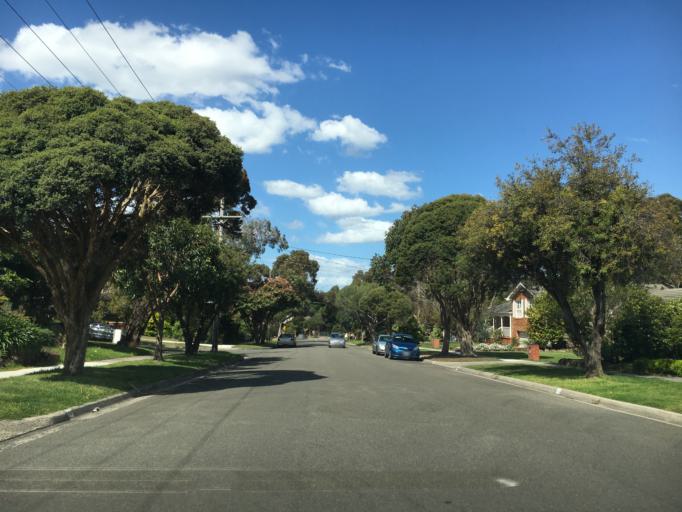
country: AU
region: Victoria
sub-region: Monash
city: Mulgrave
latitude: -37.8943
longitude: 145.1879
